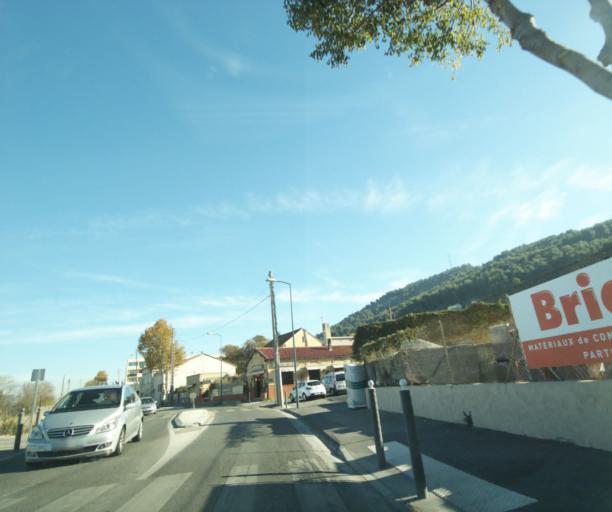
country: FR
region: Provence-Alpes-Cote d'Azur
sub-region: Departement des Bouches-du-Rhone
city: La Penne-sur-Huveaune
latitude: 43.2847
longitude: 5.4838
